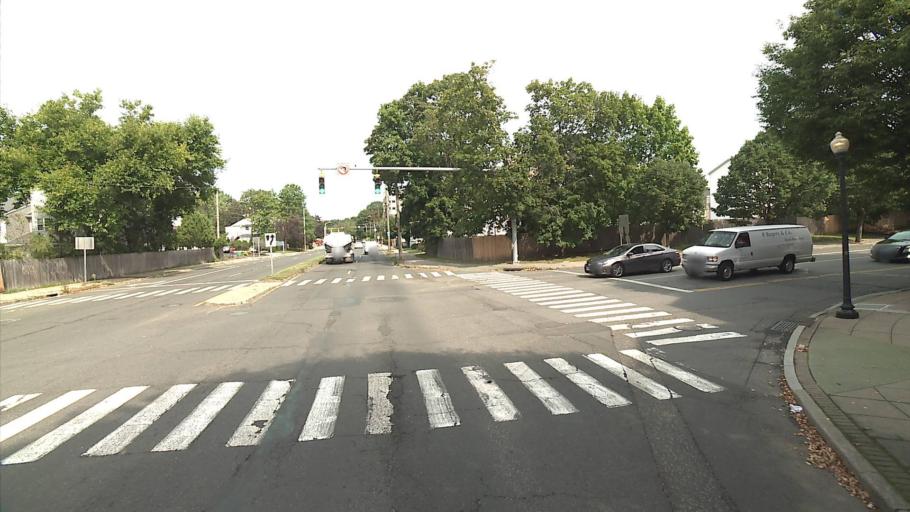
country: US
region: Connecticut
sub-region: Fairfield County
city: Stamford
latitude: 41.0601
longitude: -73.5436
